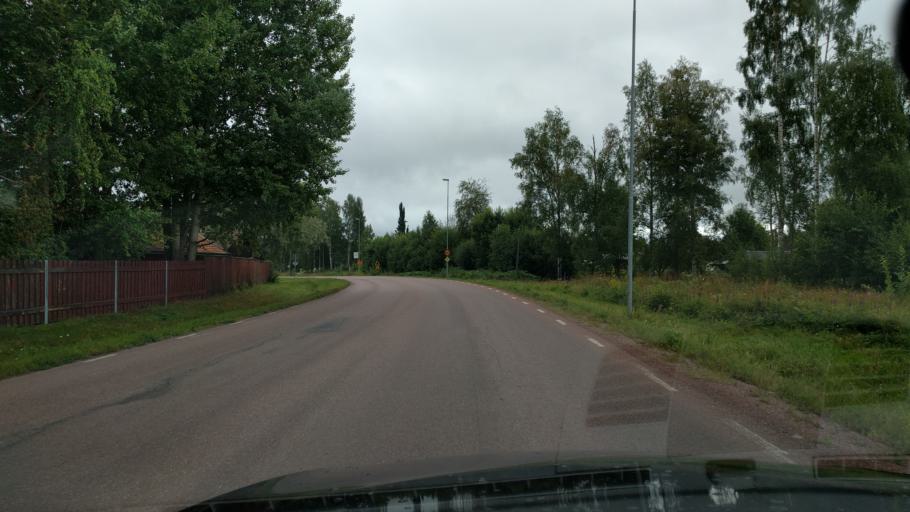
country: SE
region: Dalarna
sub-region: Mora Kommun
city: Mora
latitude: 61.0027
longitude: 14.5301
